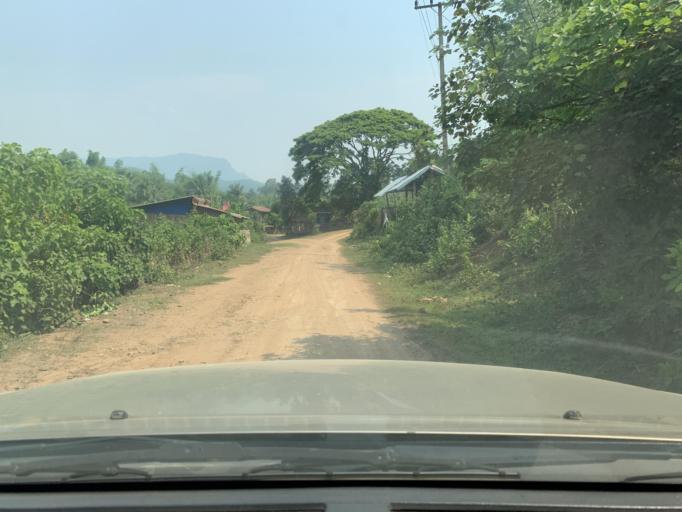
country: LA
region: Louangphabang
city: Louangphabang
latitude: 19.9353
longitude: 102.1500
